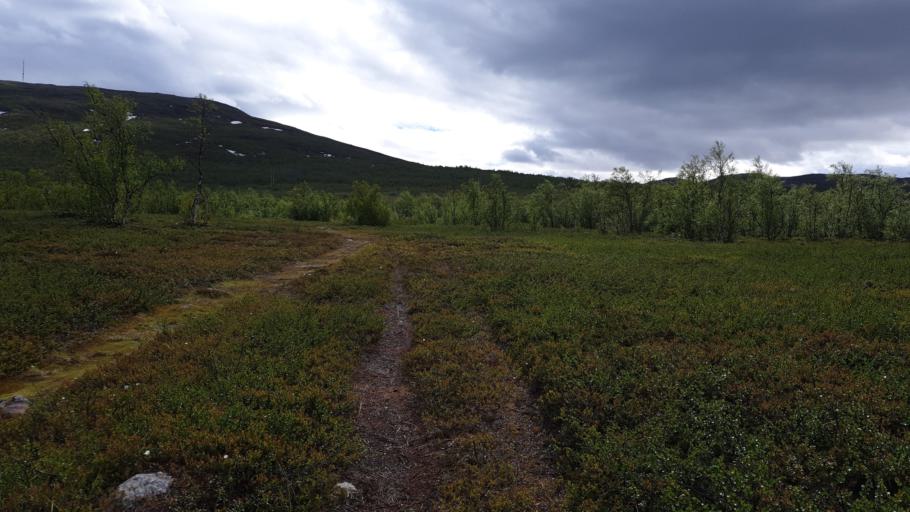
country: SE
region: Norrbotten
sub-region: Kiruna Kommun
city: Kiruna
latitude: 68.2335
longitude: 19.6191
